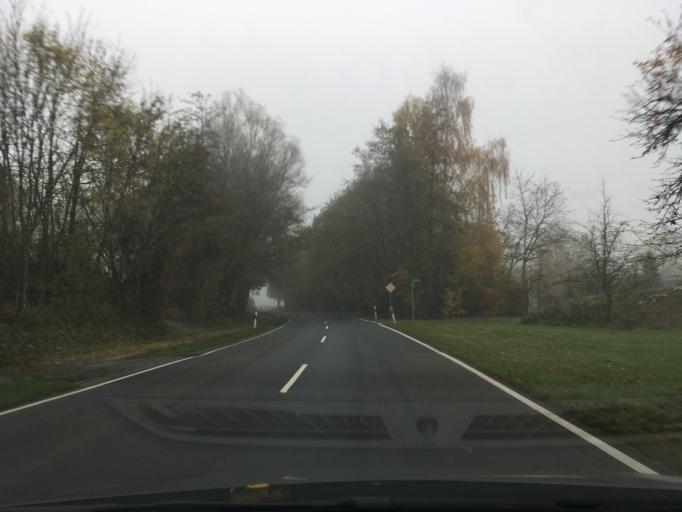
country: DE
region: North Rhine-Westphalia
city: Stadtlohn
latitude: 52.0668
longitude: 6.9279
